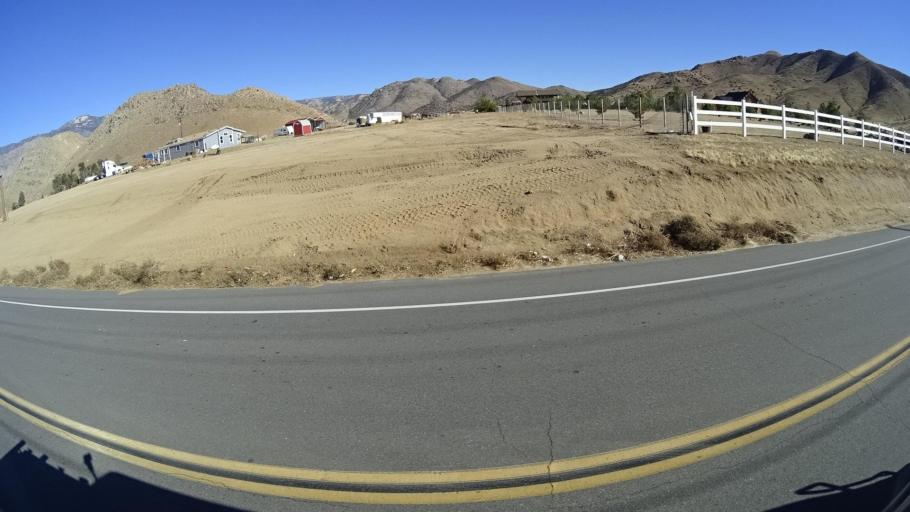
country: US
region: California
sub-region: Kern County
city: Wofford Heights
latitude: 35.7056
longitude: -118.4236
